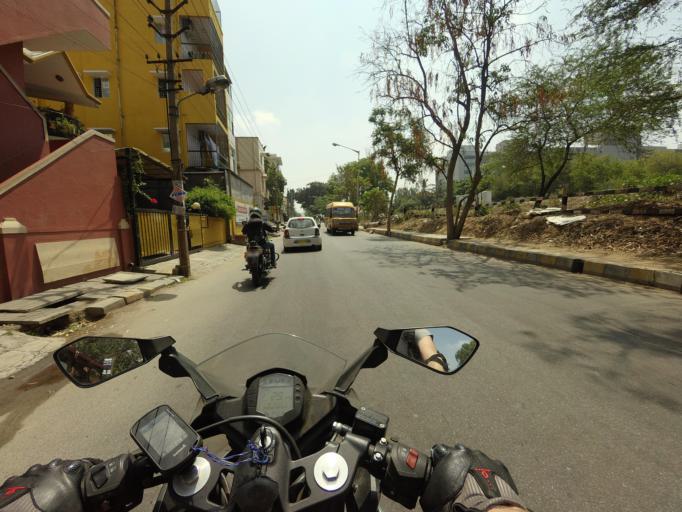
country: IN
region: Karnataka
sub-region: Bangalore Urban
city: Bangalore
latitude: 12.9950
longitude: 77.6591
